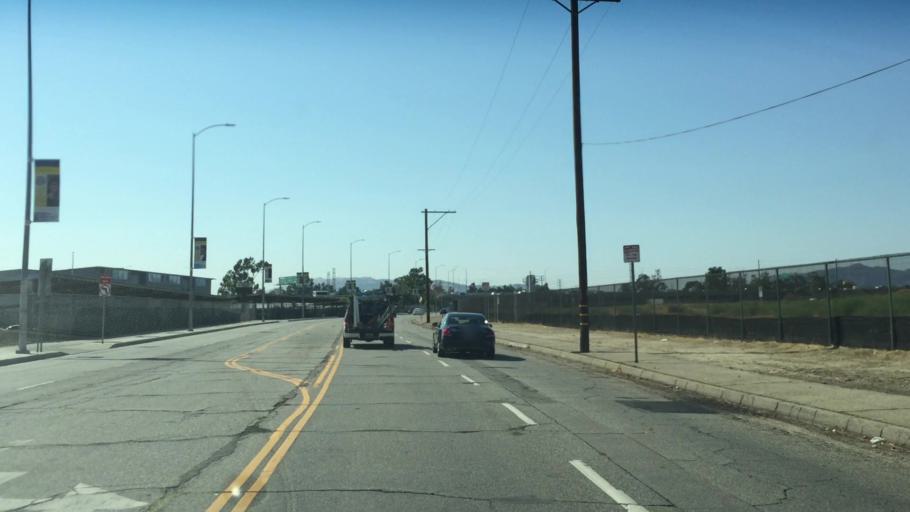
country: US
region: California
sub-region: Los Angeles County
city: Van Nuys
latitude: 34.2246
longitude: -118.4076
